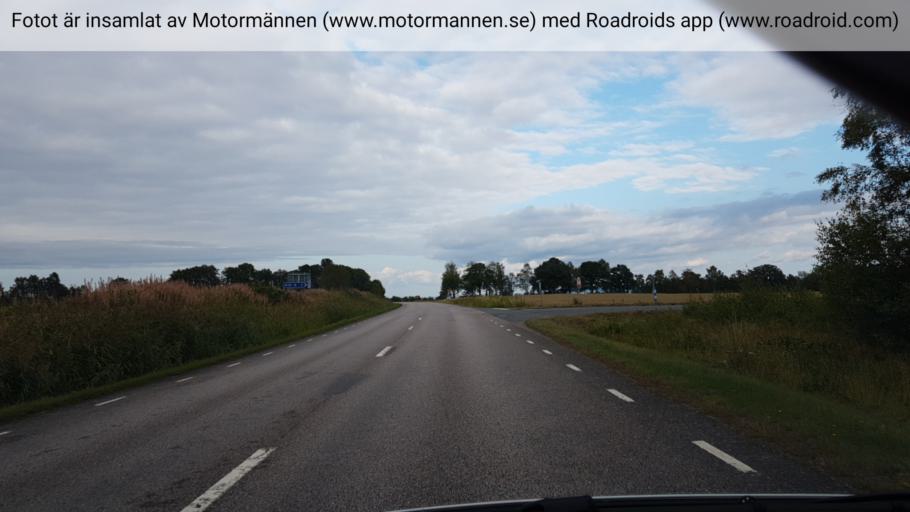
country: SE
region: Vaestra Goetaland
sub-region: Hjo Kommun
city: Hjo
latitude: 58.3230
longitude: 14.3127
